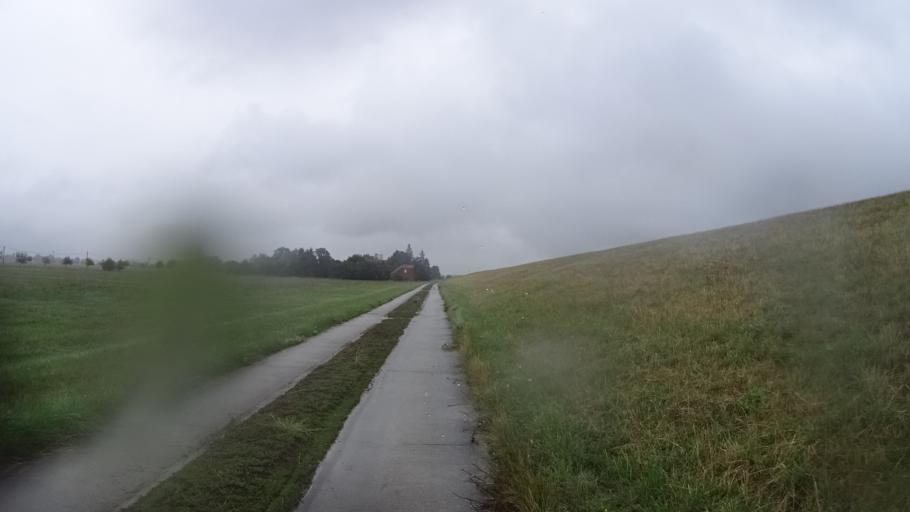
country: DE
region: Lower Saxony
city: Dannenberg
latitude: 53.1549
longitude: 11.1104
